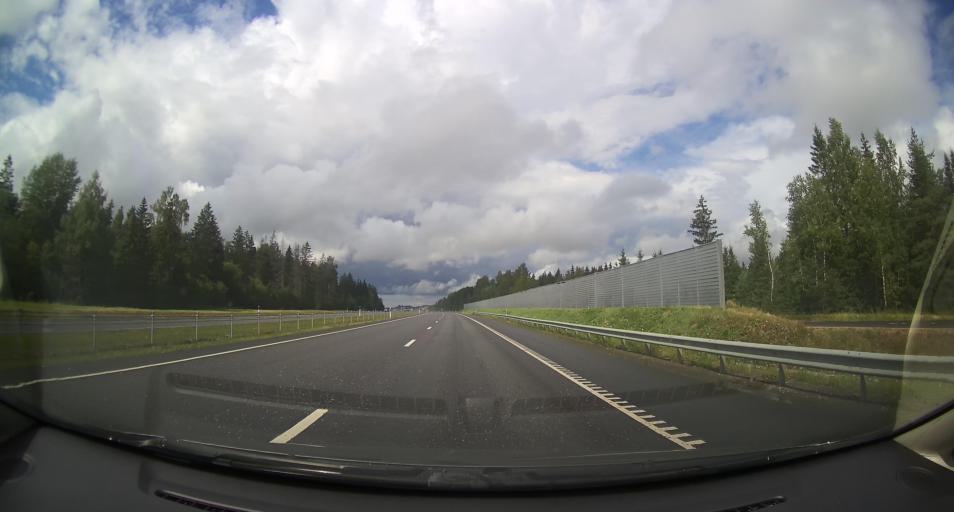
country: EE
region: Harju
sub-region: Rae vald
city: Vaida
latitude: 59.2398
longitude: 25.0281
